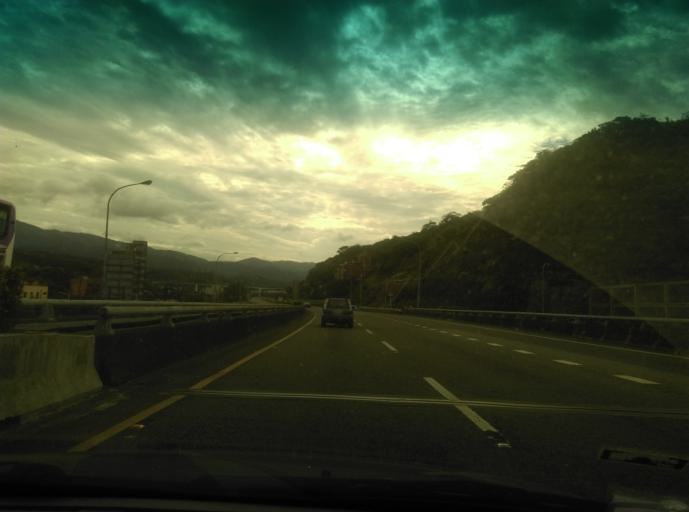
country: TW
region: Taiwan
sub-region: Keelung
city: Keelung
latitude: 25.1154
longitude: 121.7286
